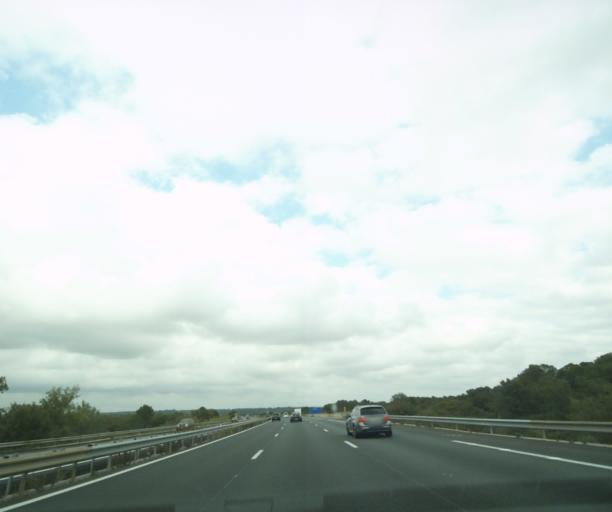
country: FR
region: Languedoc-Roussillon
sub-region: Departement de l'Herault
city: Cers
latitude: 43.3472
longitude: 3.3277
